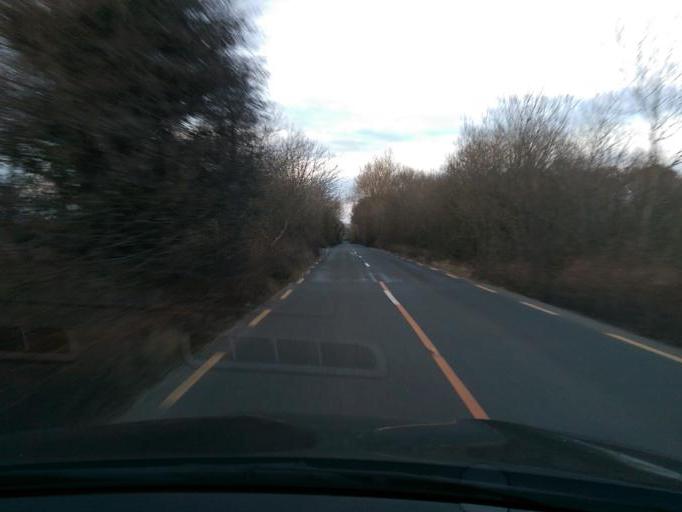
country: IE
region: Connaught
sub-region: County Galway
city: Portumna
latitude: 53.0655
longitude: -8.0886
